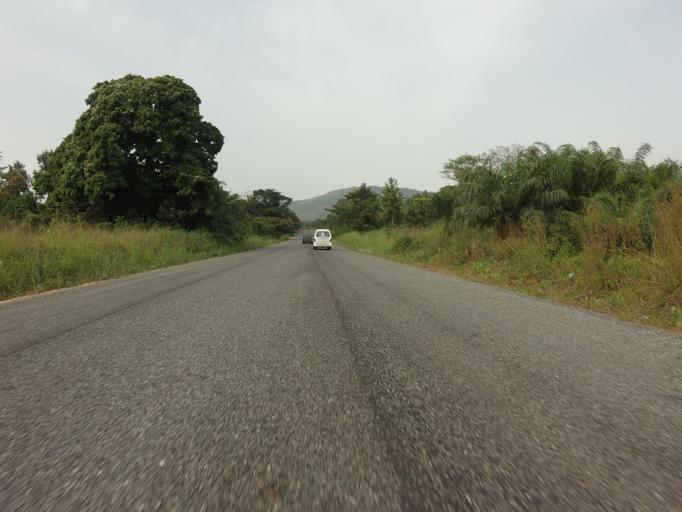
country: GH
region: Volta
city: Ho
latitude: 6.4403
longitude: 0.2027
